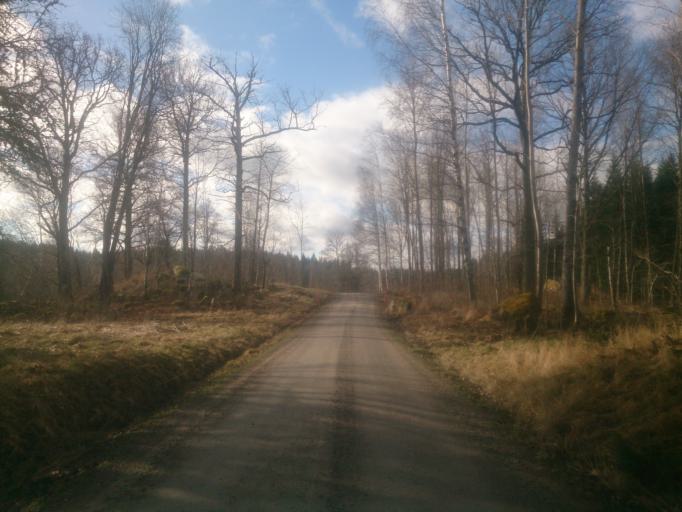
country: SE
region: OEstergoetland
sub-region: Atvidabergs Kommun
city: Atvidaberg
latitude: 58.2317
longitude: 16.1790
